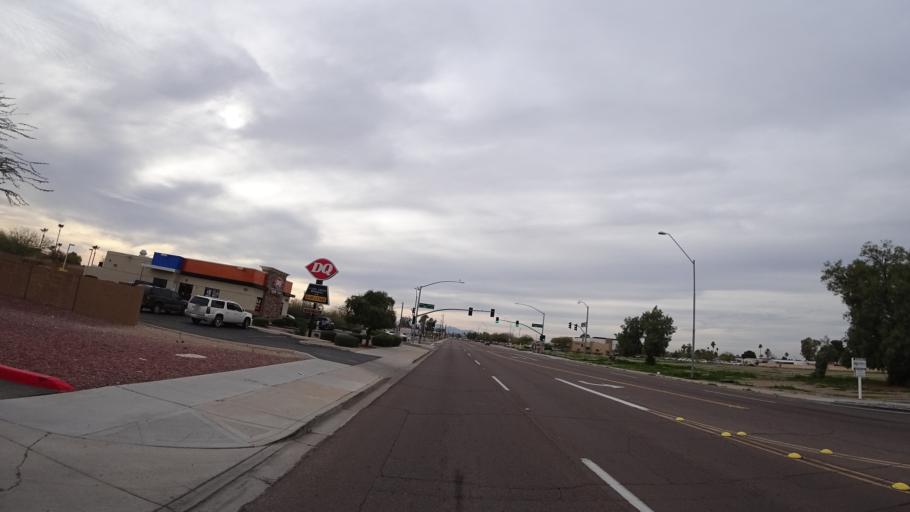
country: US
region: Arizona
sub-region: Maricopa County
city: Peoria
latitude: 33.5808
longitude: -112.2501
